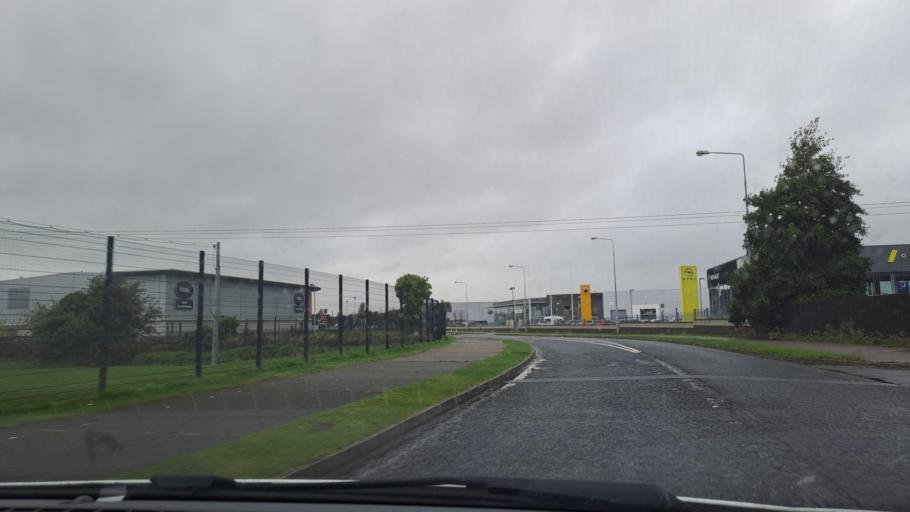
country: IE
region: Leinster
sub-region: Lu
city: Blackrock
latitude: 53.9884
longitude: -6.3727
